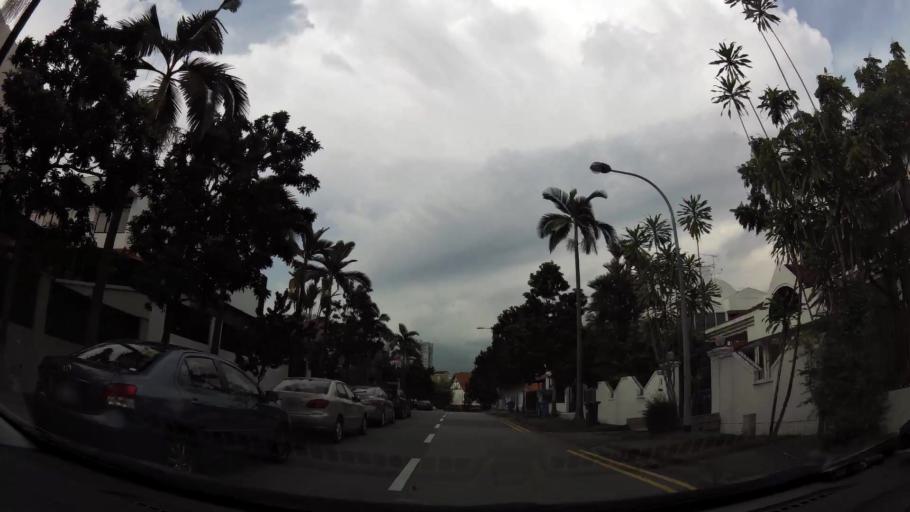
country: SG
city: Singapore
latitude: 1.3512
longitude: 103.8465
